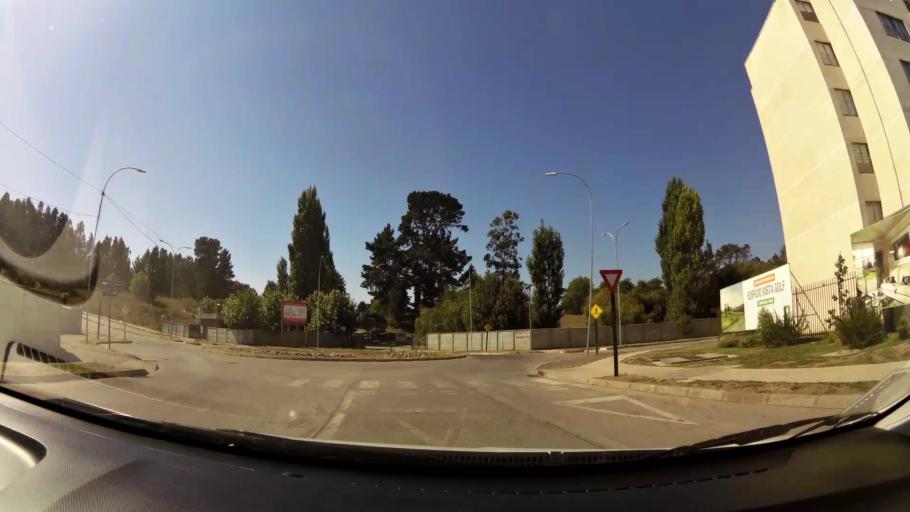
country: CL
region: Biobio
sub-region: Provincia de Concepcion
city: Concepcion
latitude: -36.7883
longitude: -73.0332
